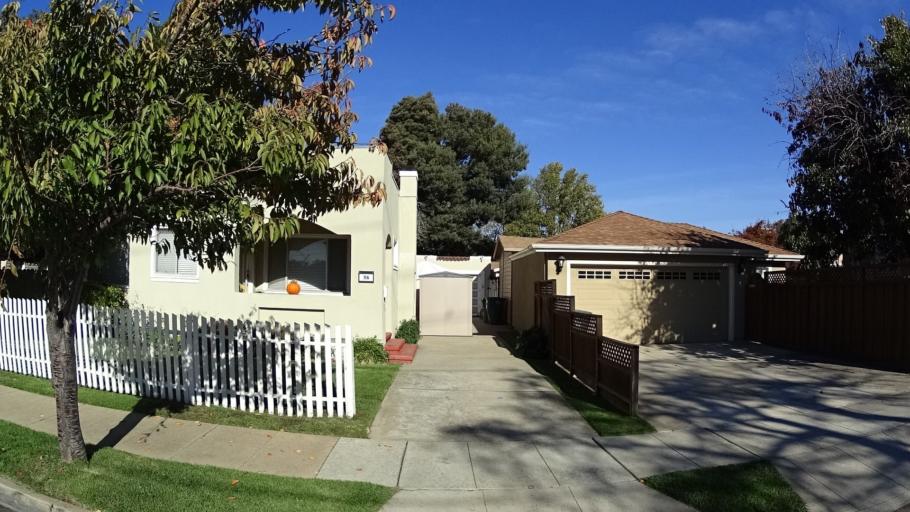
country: US
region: California
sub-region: San Mateo County
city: San Mateo
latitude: 37.5820
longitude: -122.3363
